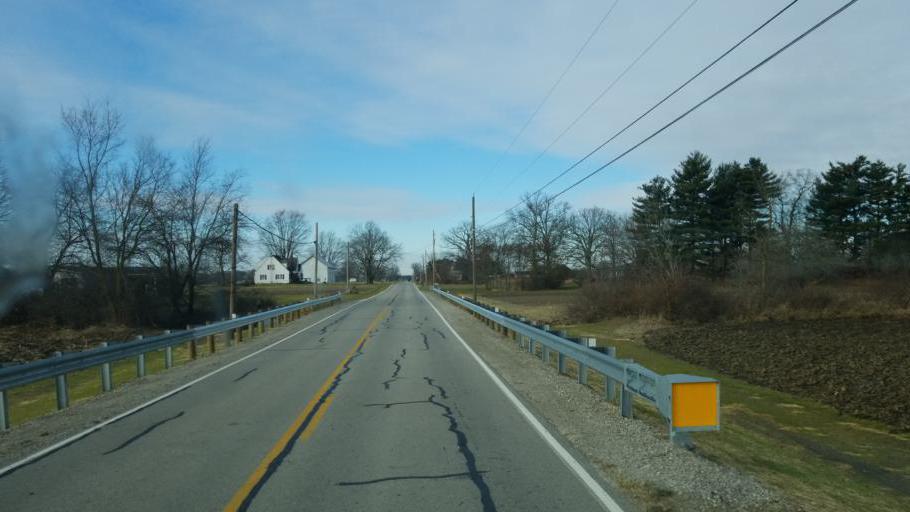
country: US
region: Ohio
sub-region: Marion County
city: Marion
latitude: 40.5642
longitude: -83.0324
